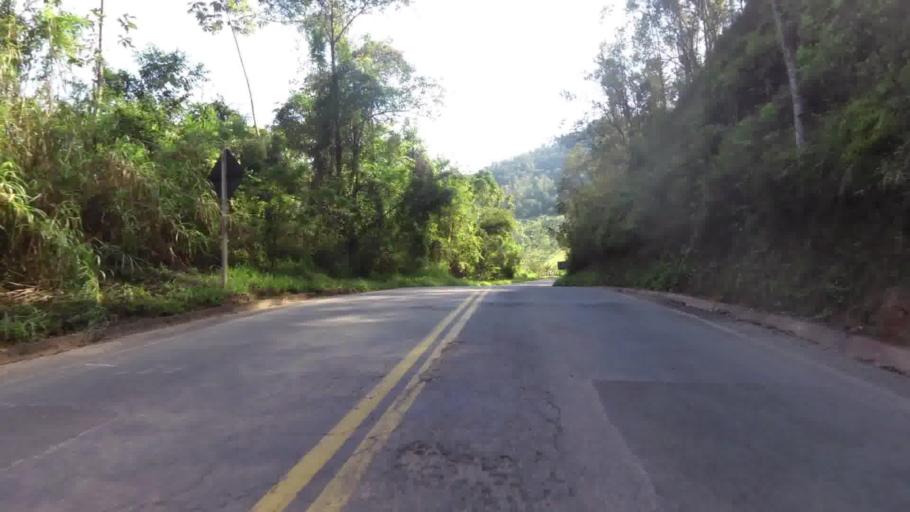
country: BR
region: Espirito Santo
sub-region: Alfredo Chaves
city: Alfredo Chaves
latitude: -20.5949
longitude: -40.7967
